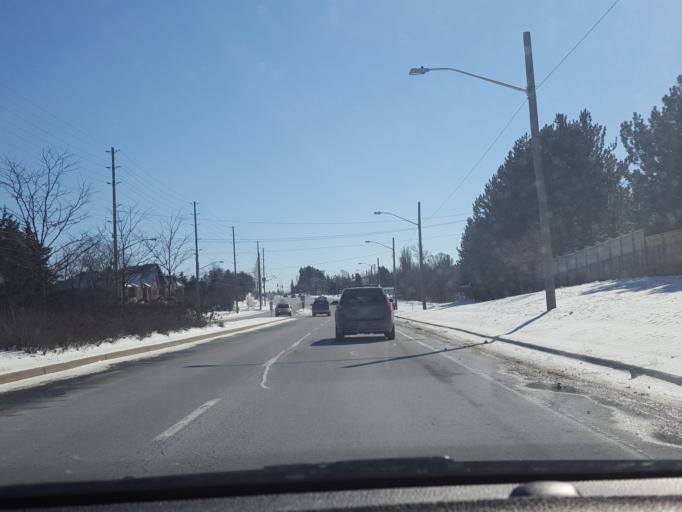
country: CA
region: Ontario
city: Waterloo
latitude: 43.4564
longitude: -80.5567
